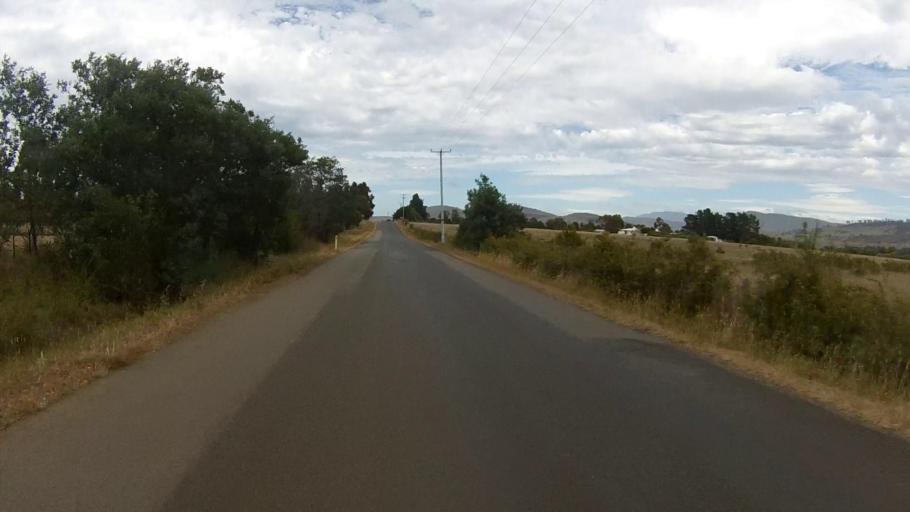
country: AU
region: Tasmania
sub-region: Clarence
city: Cambridge
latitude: -42.7159
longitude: 147.4523
